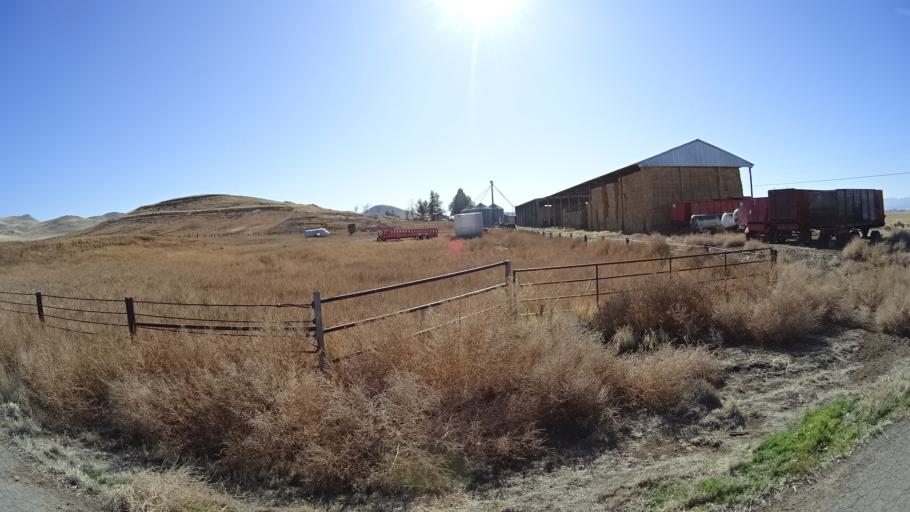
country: US
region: California
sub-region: Siskiyou County
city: Montague
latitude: 41.7937
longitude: -122.4334
